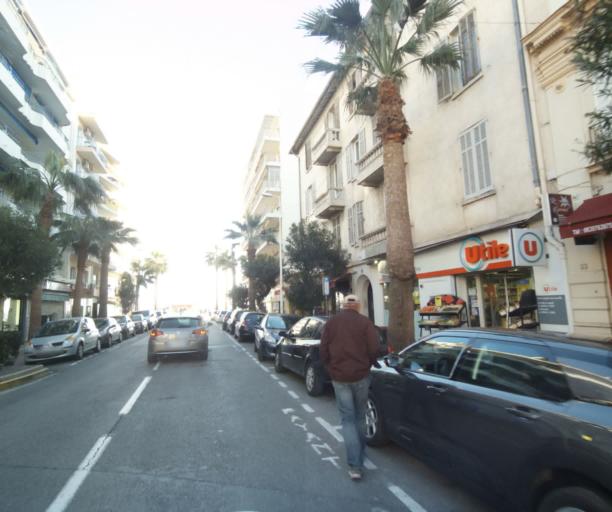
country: FR
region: Provence-Alpes-Cote d'Azur
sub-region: Departement des Alpes-Maritimes
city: Antibes
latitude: 43.5698
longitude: 7.1086
